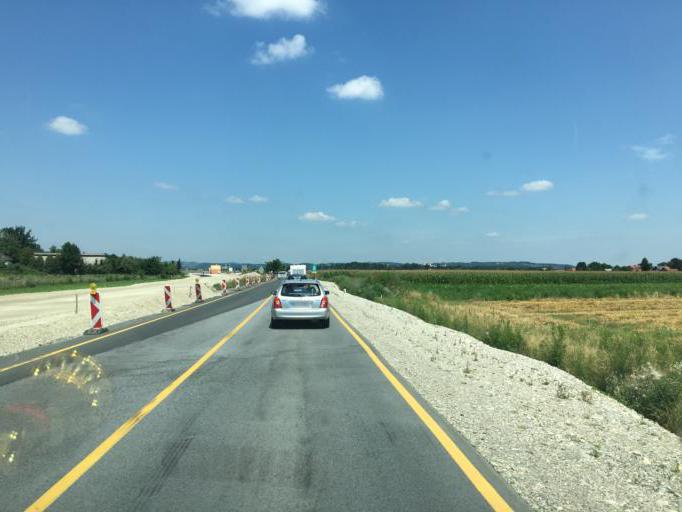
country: SI
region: Hajdina
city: Spodnja Hajdina
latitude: 46.3826
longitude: 15.8657
